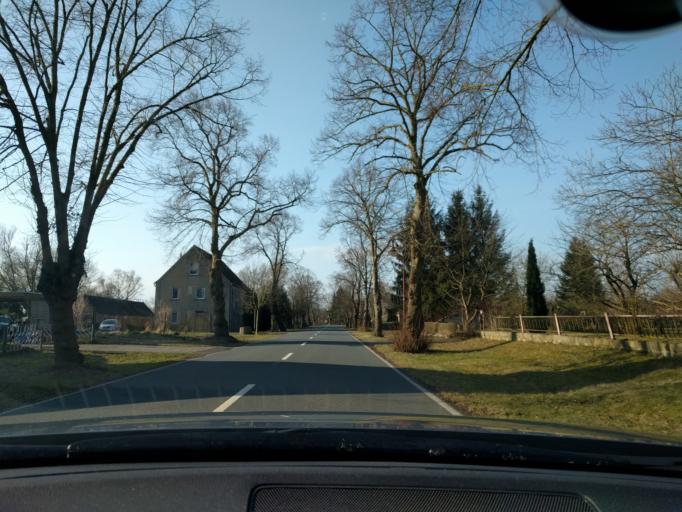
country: DE
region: Saxony-Anhalt
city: Iden
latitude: 52.7557
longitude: 11.9349
